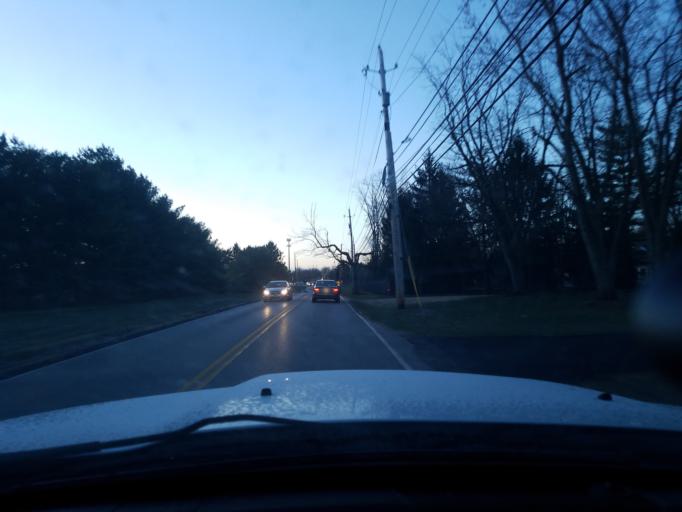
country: US
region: Indiana
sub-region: Marion County
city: Meridian Hills
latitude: 39.9290
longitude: -86.1840
